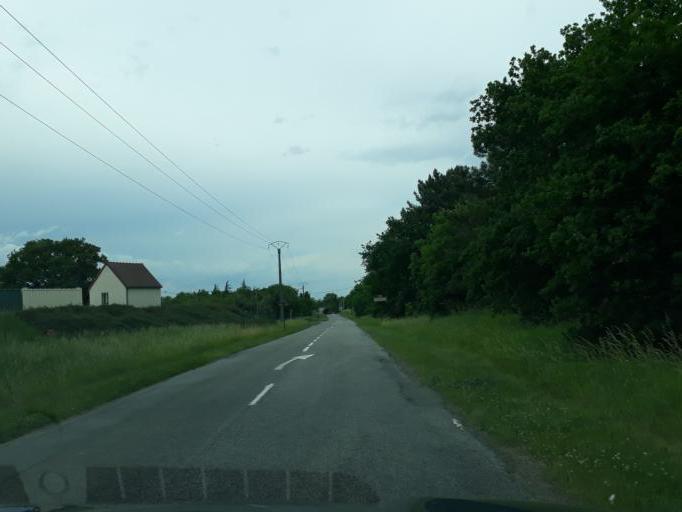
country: FR
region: Centre
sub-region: Departement du Loiret
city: Jargeau
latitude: 47.8525
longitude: 2.1320
